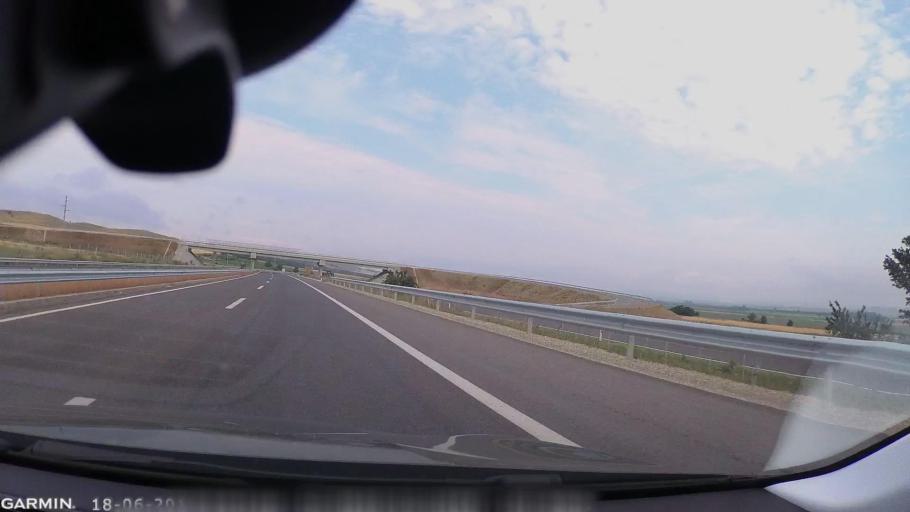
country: MK
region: Stip
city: Shtip
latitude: 41.7902
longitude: 22.1075
